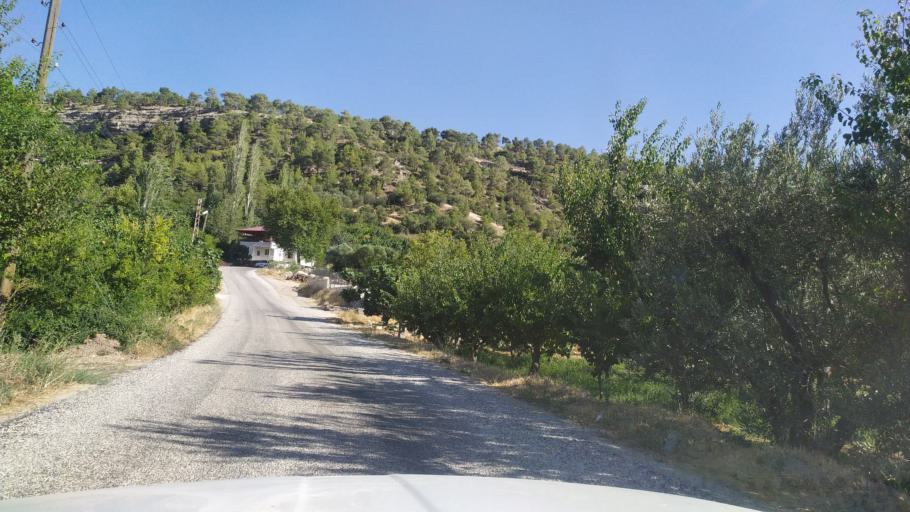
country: TR
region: Mersin
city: Mut
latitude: 36.7063
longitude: 33.4733
